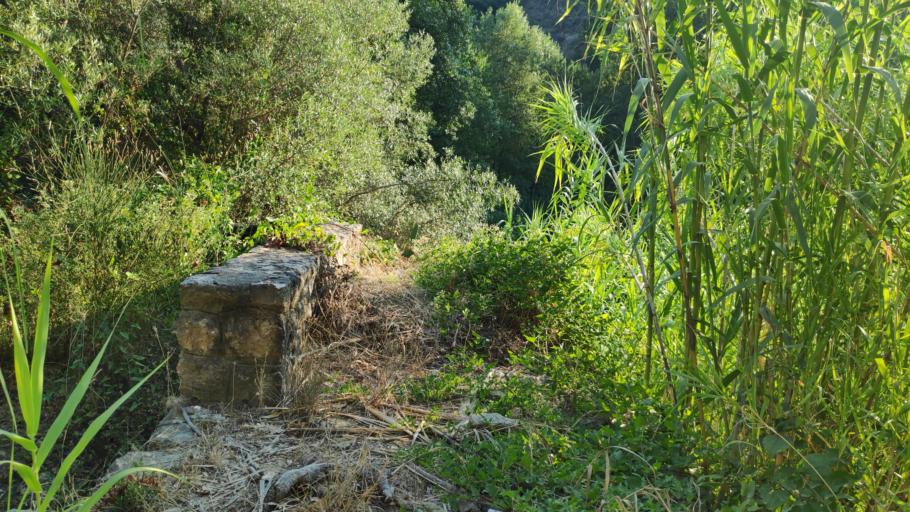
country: IT
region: Calabria
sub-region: Provincia di Reggio Calabria
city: Placanica
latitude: 38.4142
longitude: 16.4386
